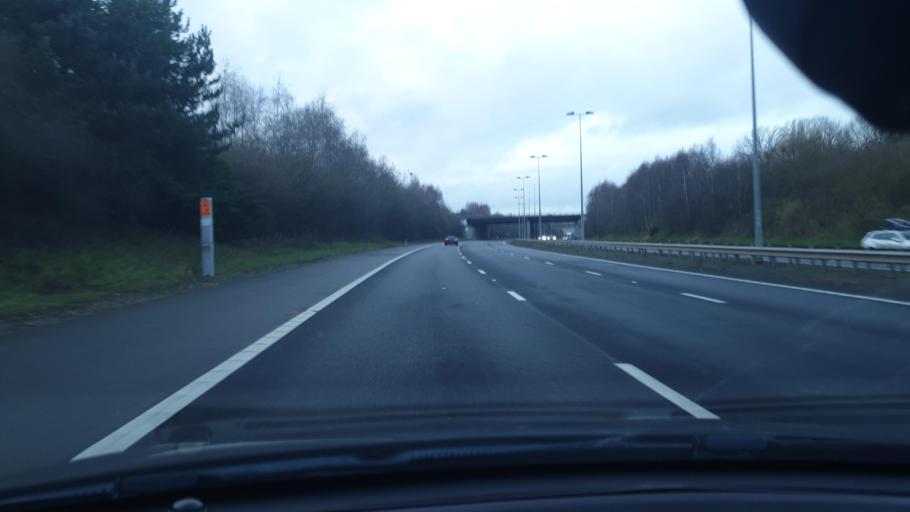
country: GB
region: England
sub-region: Solihull
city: Chelmsley Wood
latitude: 52.4805
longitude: -1.7033
